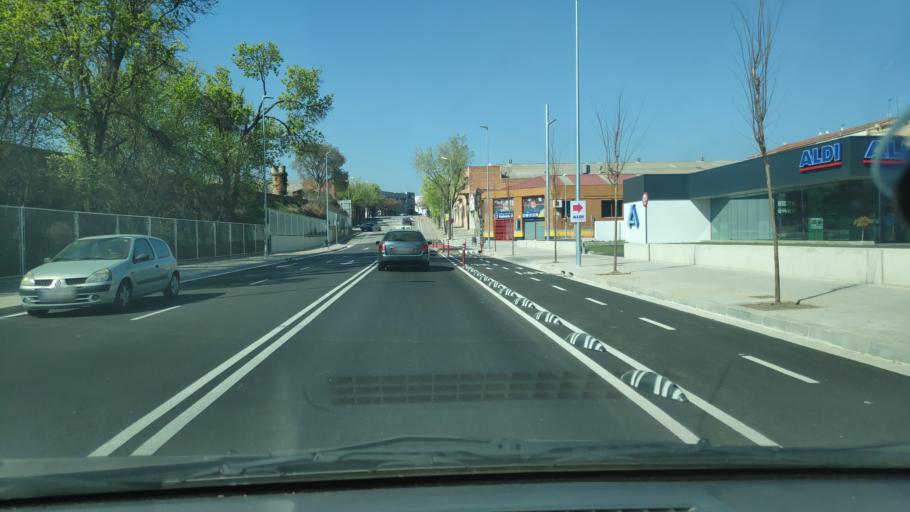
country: ES
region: Catalonia
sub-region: Provincia de Barcelona
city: Sant Quirze del Valles
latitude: 41.5396
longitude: 2.0950
